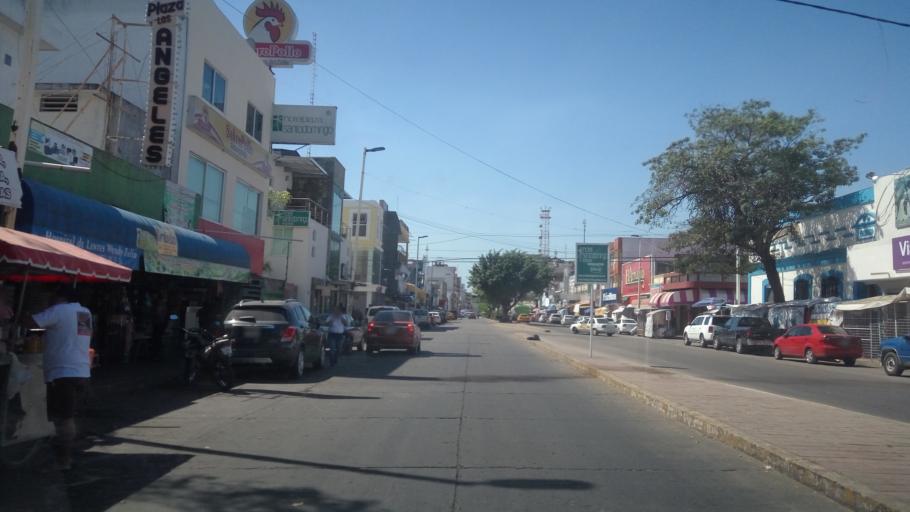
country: MX
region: Tabasco
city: Villahermosa
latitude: 17.9942
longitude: -92.9165
